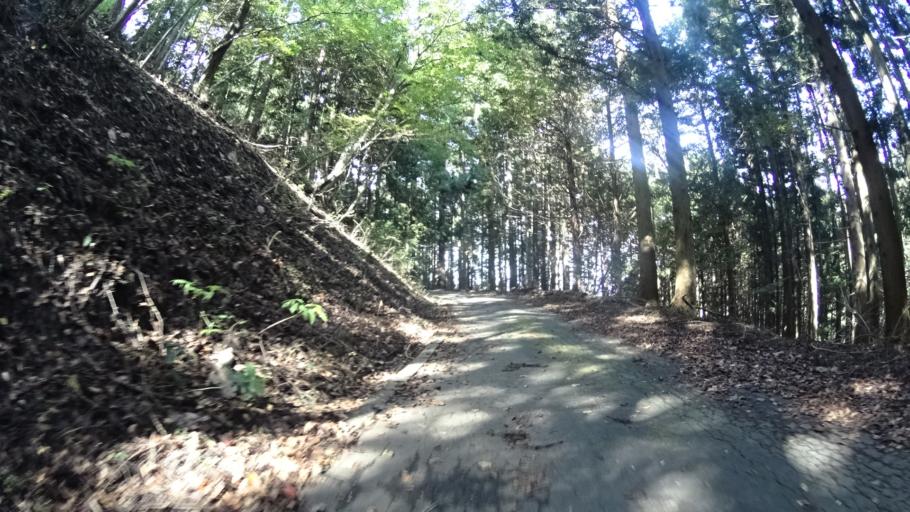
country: JP
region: Yamanashi
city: Otsuki
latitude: 35.5792
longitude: 138.9770
